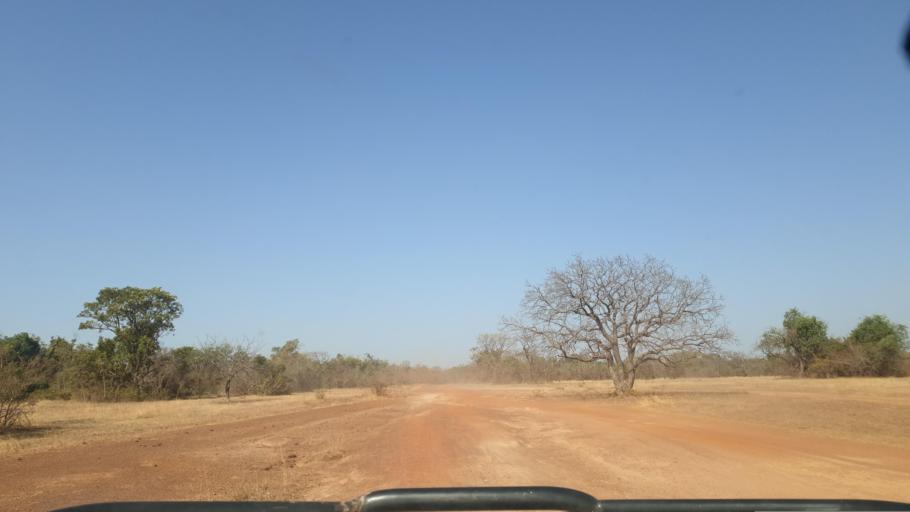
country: ML
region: Sikasso
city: Bougouni
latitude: 11.8200
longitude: -6.9495
